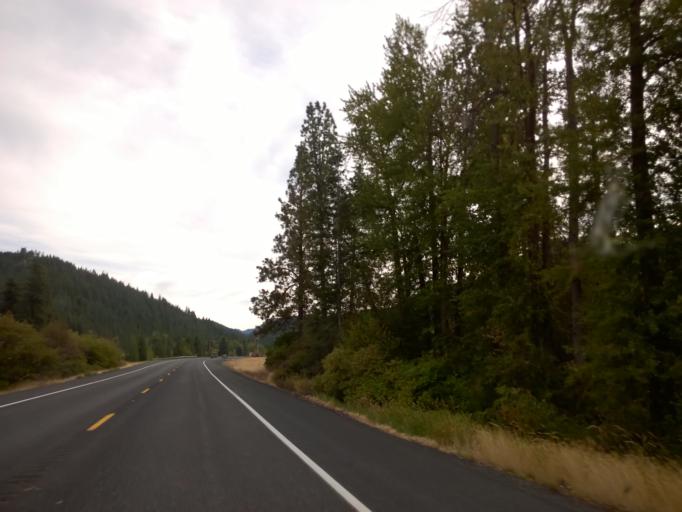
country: US
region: Washington
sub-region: Chelan County
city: Leavenworth
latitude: 47.5180
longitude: -120.6269
